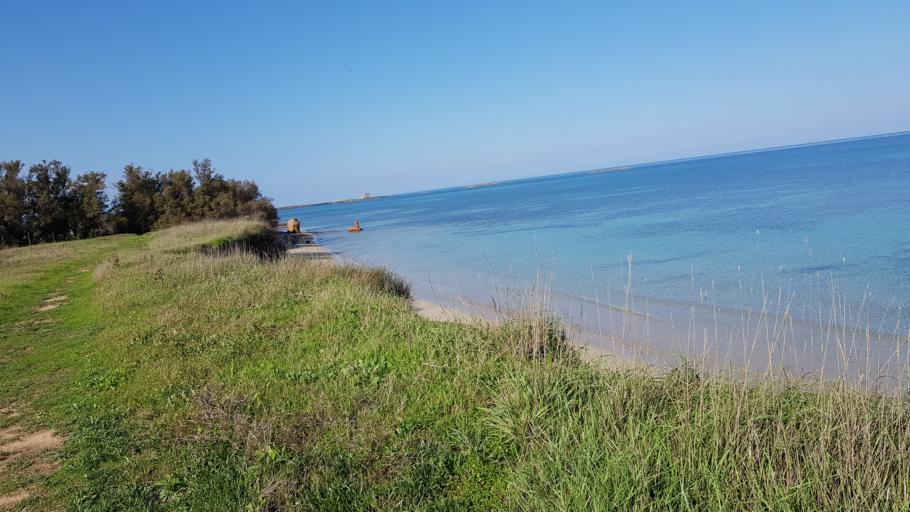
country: IT
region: Apulia
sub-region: Provincia di Brindisi
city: San Vito dei Normanni
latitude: 40.7007
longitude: 17.8148
